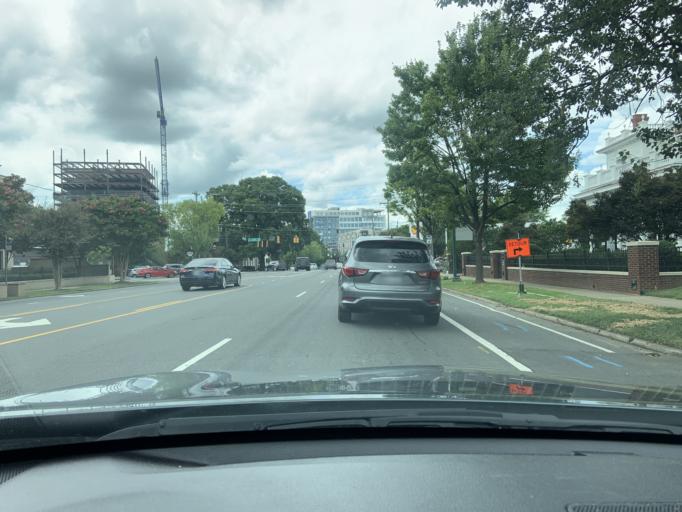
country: US
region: North Carolina
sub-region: Mecklenburg County
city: Charlotte
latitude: 35.2113
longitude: -80.8569
